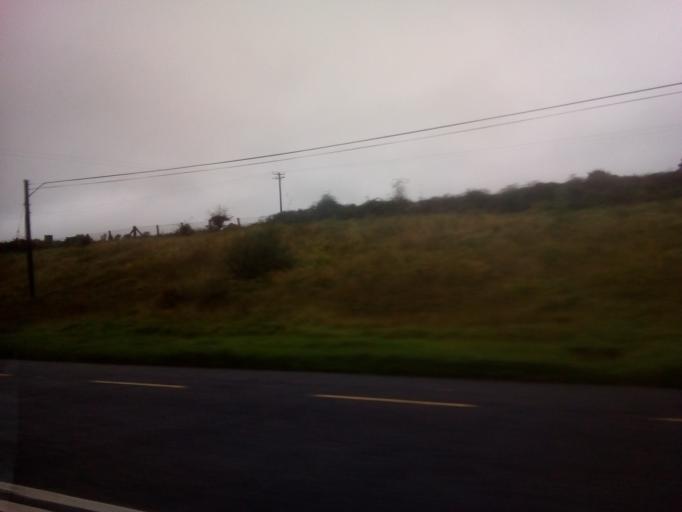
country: IE
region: Leinster
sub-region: An Iarmhi
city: An Muileann gCearr
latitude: 53.6066
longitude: -7.4301
